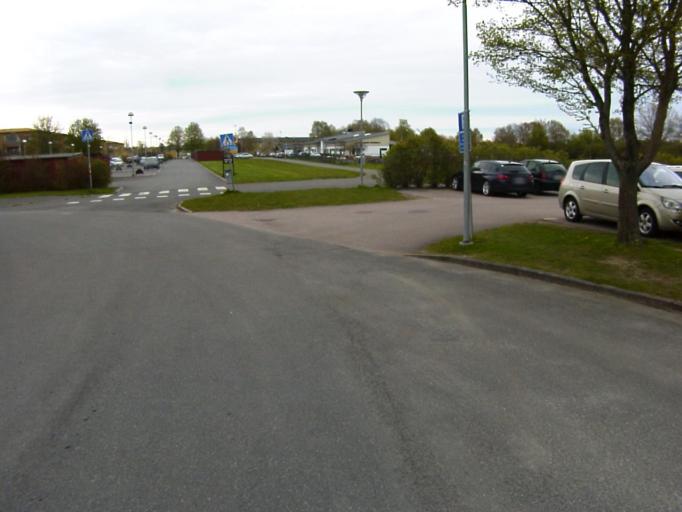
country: SE
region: Skane
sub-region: Kristianstads Kommun
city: Kristianstad
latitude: 56.0188
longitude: 14.1280
